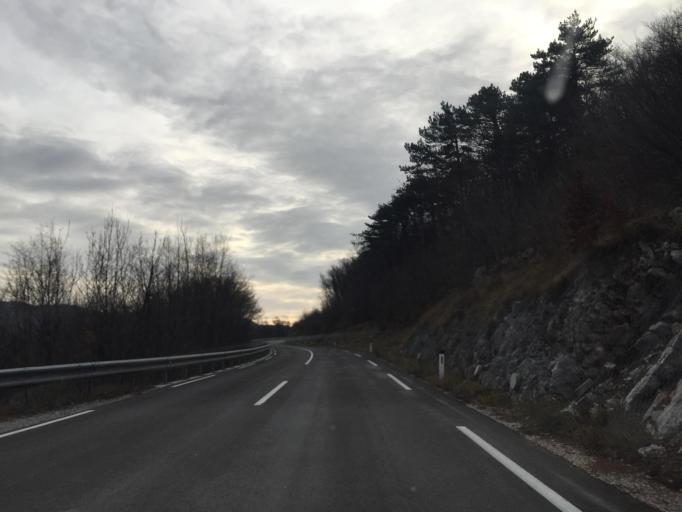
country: SI
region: Nova Gorica
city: Kromberk
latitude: 45.9881
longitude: 13.6744
